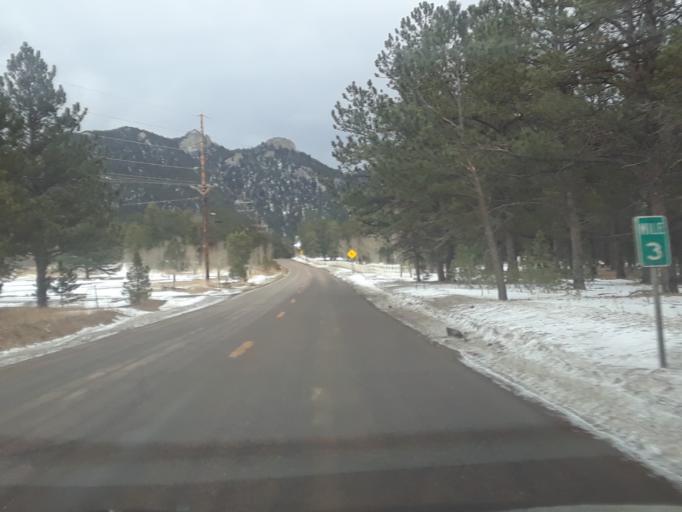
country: US
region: Colorado
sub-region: Gilpin County
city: Central City
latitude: 39.8397
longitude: -105.4475
